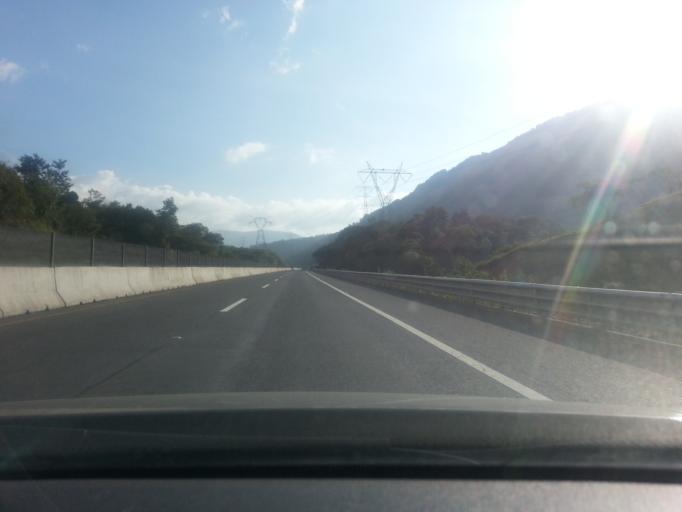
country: MX
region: Puebla
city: Xicotepec de Juarez
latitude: 20.2707
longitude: -97.9971
